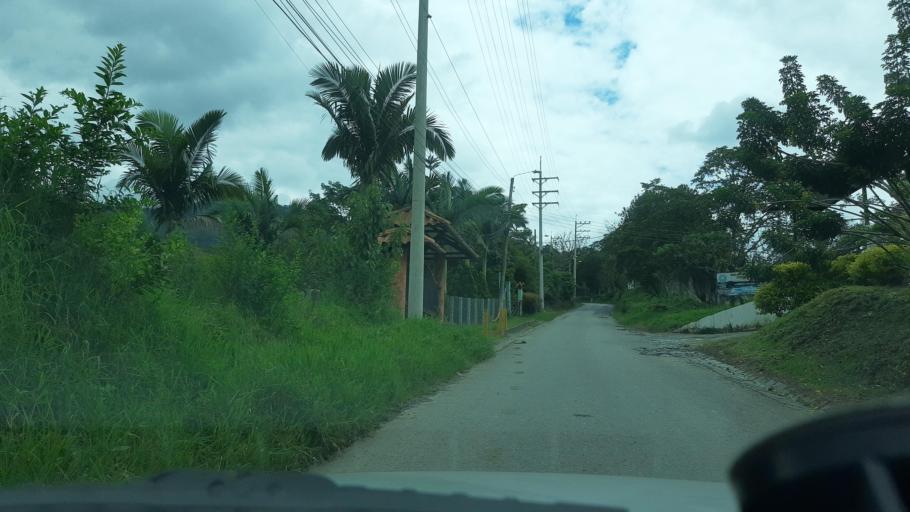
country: CO
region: Boyaca
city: Moniquira
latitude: 5.8769
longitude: -73.5783
